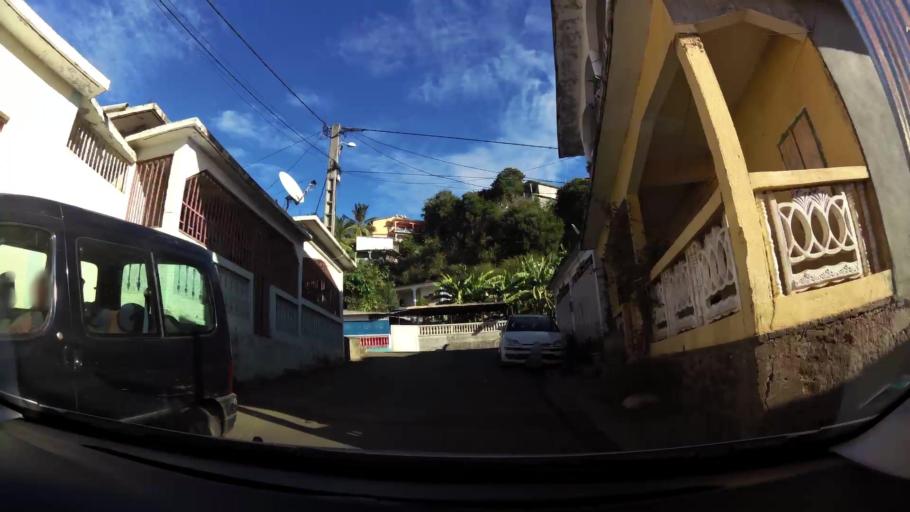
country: YT
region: Koungou
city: Koungou
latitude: -12.7449
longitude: 45.2207
